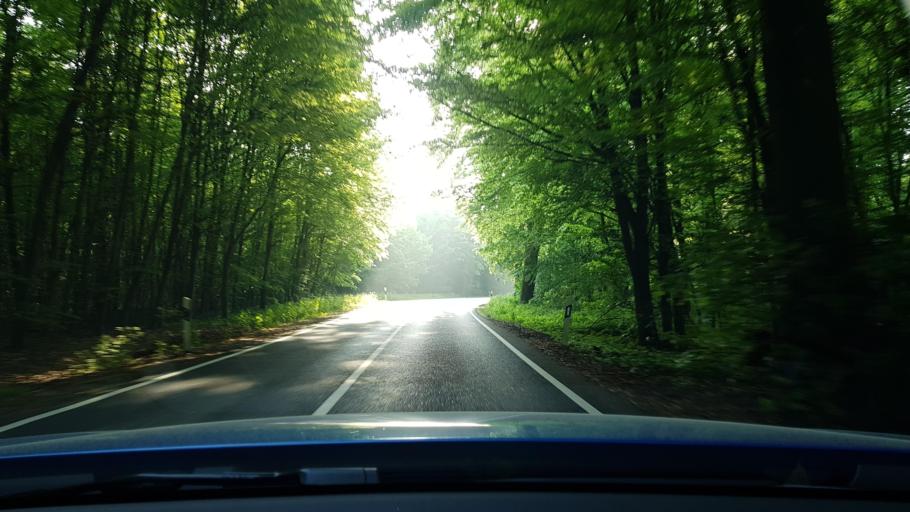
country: LU
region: Luxembourg
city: Heisdorf-sur-Alzette
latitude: 49.6594
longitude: 6.1882
